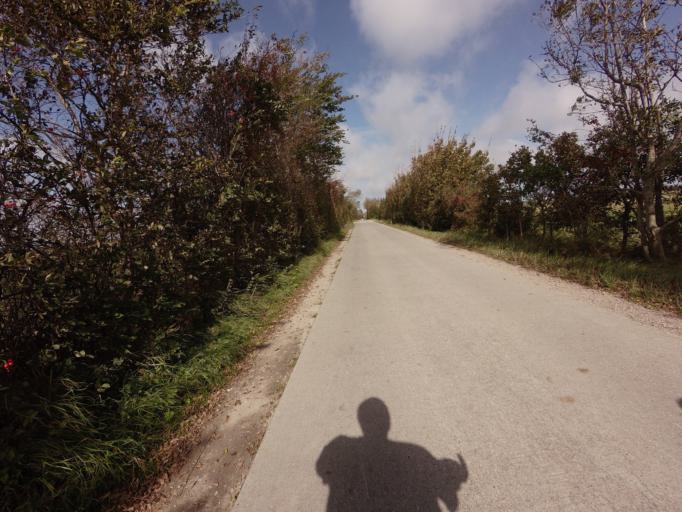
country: NL
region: Zeeland
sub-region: Gemeente Middelburg
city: Middelburg
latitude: 51.5311
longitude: 3.5270
